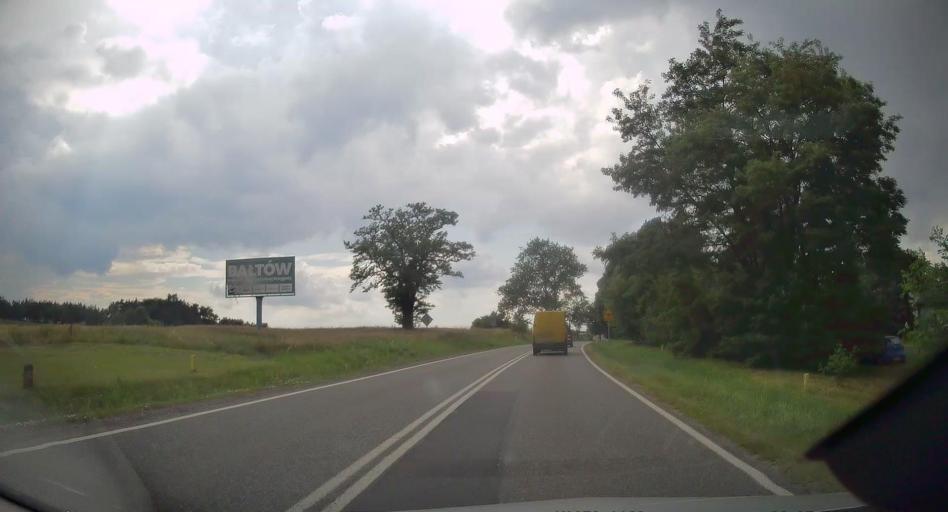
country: PL
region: Lodz Voivodeship
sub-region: Powiat skierniewicki
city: Gluchow
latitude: 51.7712
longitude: 20.1486
